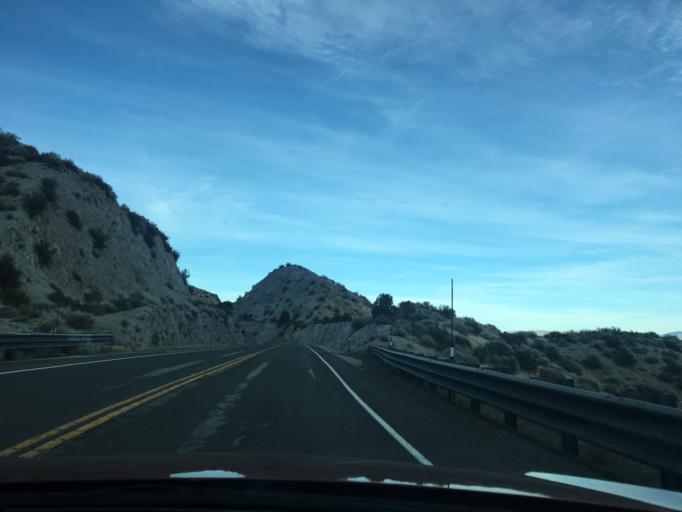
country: US
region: Nevada
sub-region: Douglas County
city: Kingsbury
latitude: 38.9544
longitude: -119.8485
